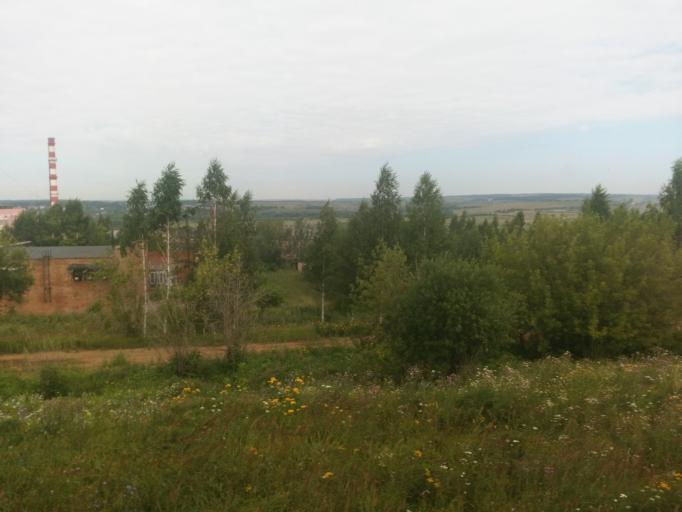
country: RU
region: Tatarstan
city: Mendeleyevsk
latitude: 55.9000
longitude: 52.3306
